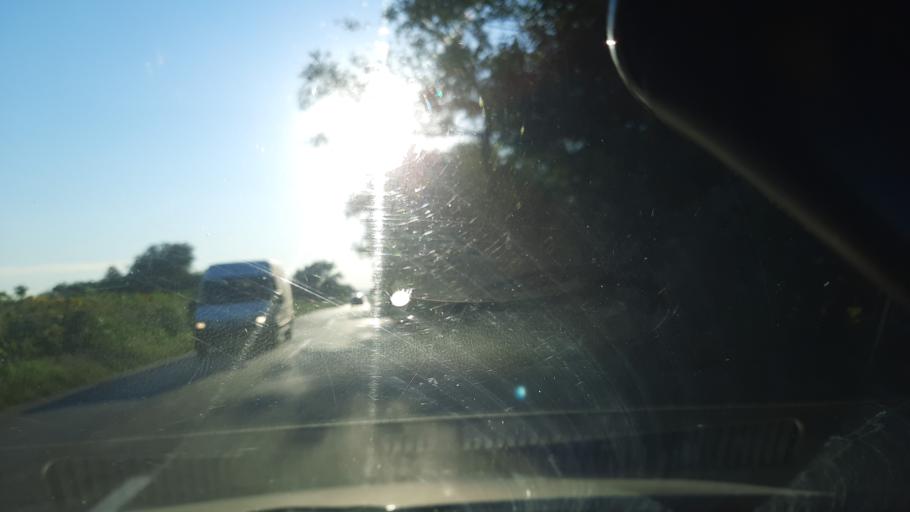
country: RS
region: Central Serbia
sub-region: Branicevski Okrug
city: Malo Crnice
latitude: 44.5758
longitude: 21.3450
